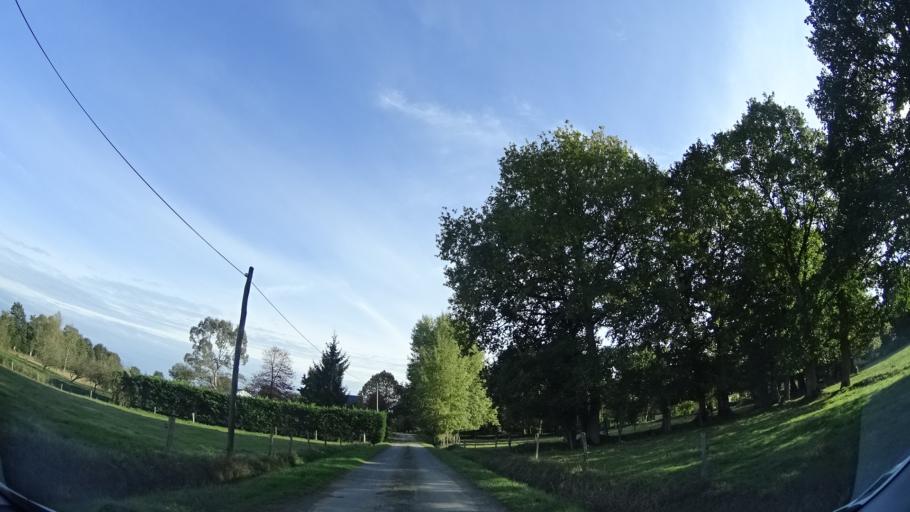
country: FR
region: Brittany
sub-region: Departement d'Ille-et-Vilaine
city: Geveze
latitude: 48.2158
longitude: -1.8221
